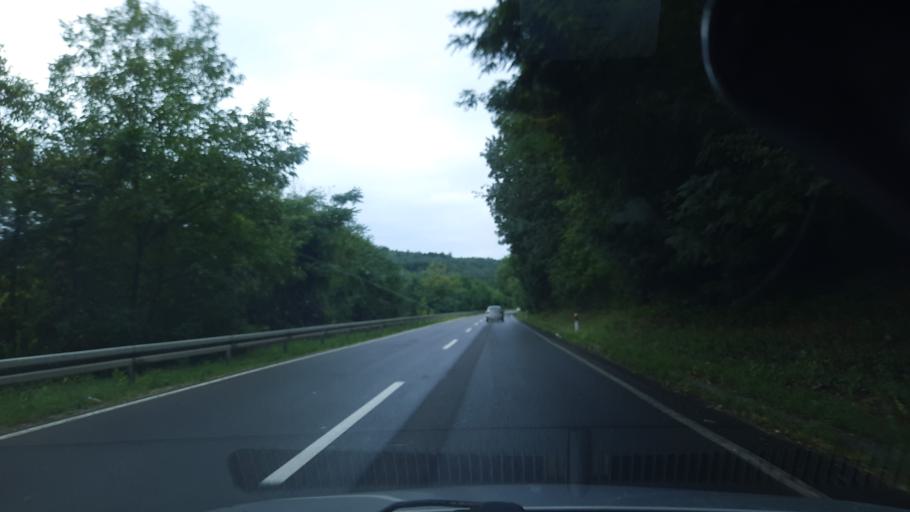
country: RS
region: Central Serbia
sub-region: Sumadijski Okrug
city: Knic
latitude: 43.9664
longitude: 20.8101
